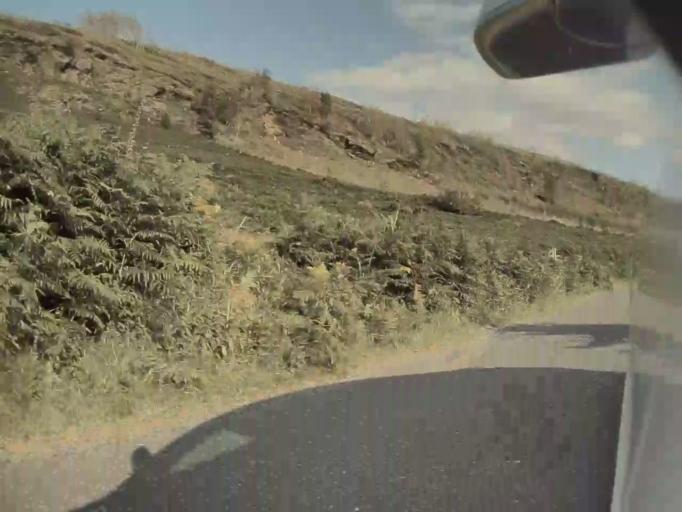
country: IE
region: Leinster
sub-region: Wicklow
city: Rathdrum
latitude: 53.0460
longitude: -6.3275
